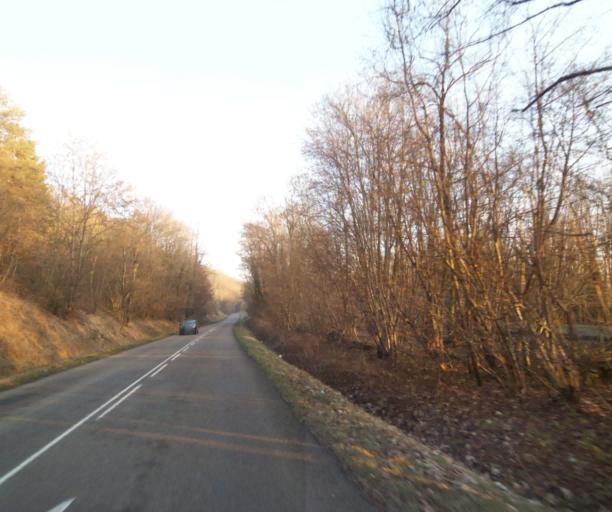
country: FR
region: Lorraine
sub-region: Departement de la Meuse
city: Ancerville
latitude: 48.6140
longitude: 5.0382
